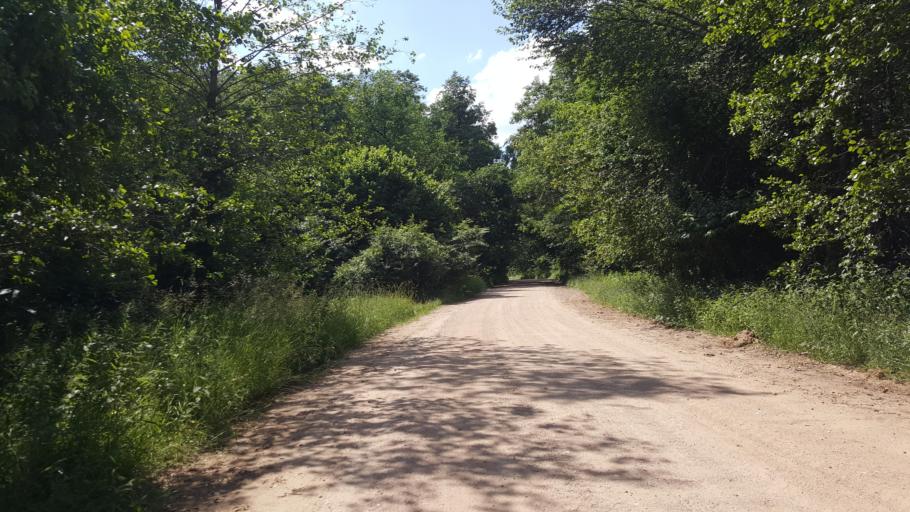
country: BY
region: Brest
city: Kamyanyuki
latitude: 52.5486
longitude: 23.6565
